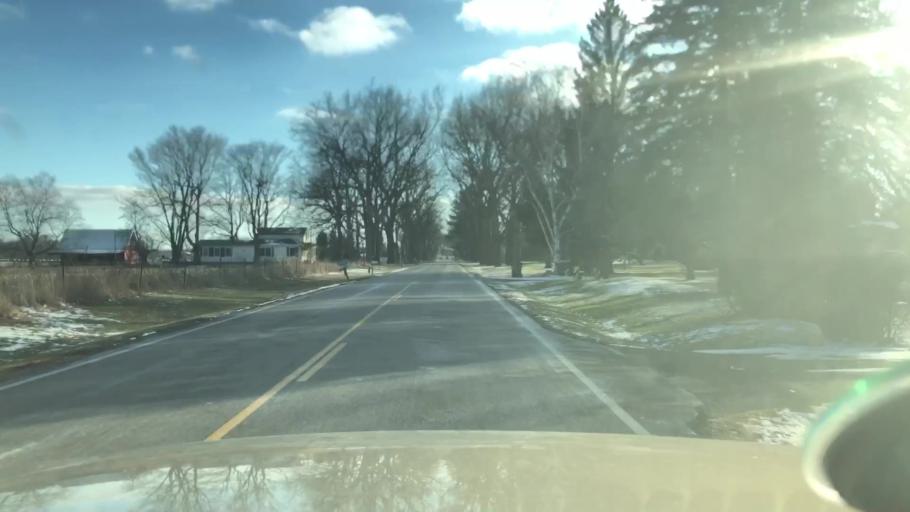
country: US
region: Michigan
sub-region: Jackson County
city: Vandercook Lake
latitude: 42.1741
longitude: -84.4521
